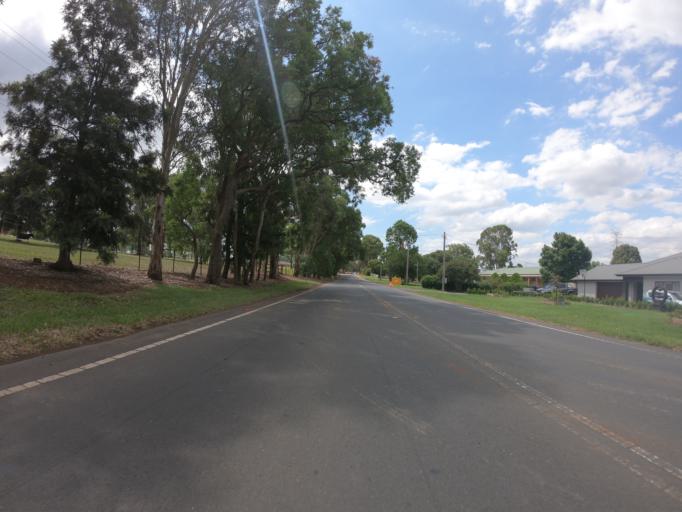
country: AU
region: New South Wales
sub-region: Penrith Municipality
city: Kingswood Park
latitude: -33.8219
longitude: 150.7609
